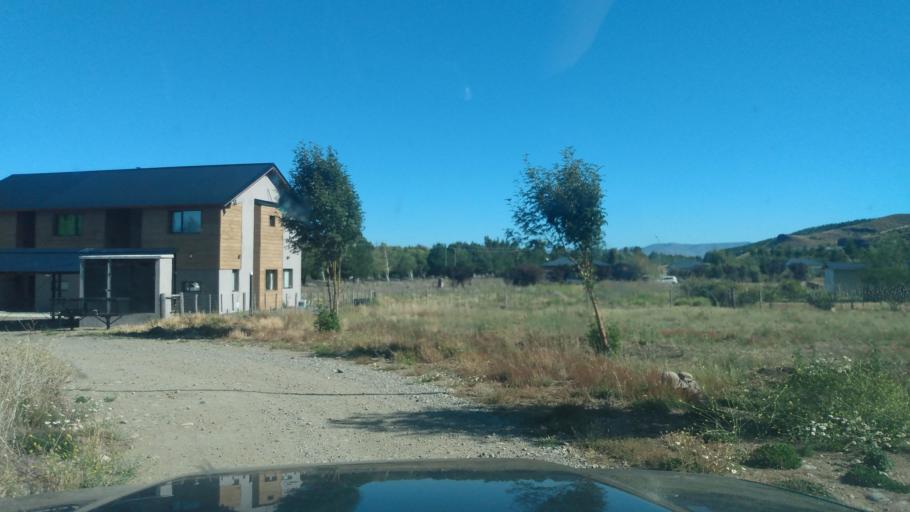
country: AR
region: Neuquen
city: Junin de los Andes
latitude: -39.9659
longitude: -71.0820
